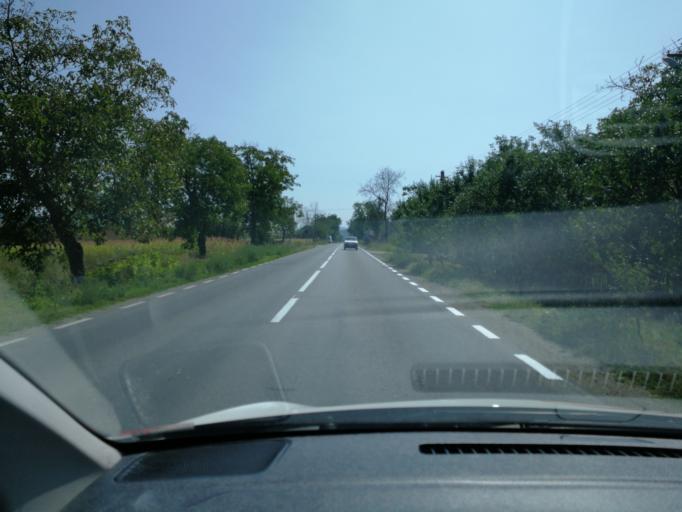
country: RO
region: Prahova
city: Drajna de Jos
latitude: 45.2367
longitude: 26.0288
